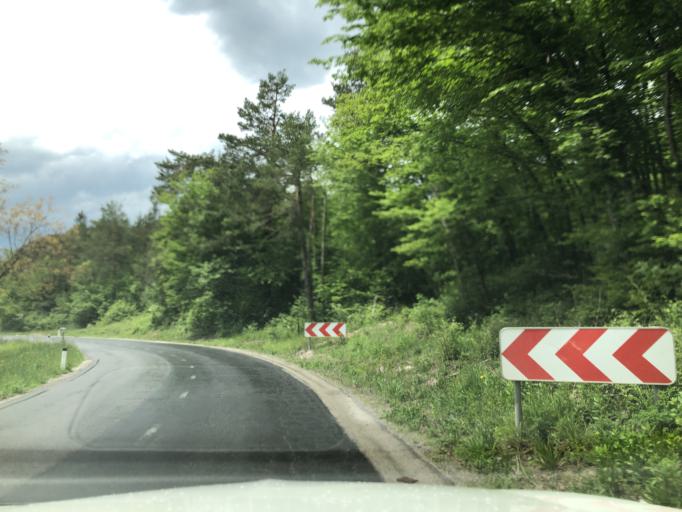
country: SI
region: Bloke
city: Nova Vas
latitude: 45.7644
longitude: 14.4353
